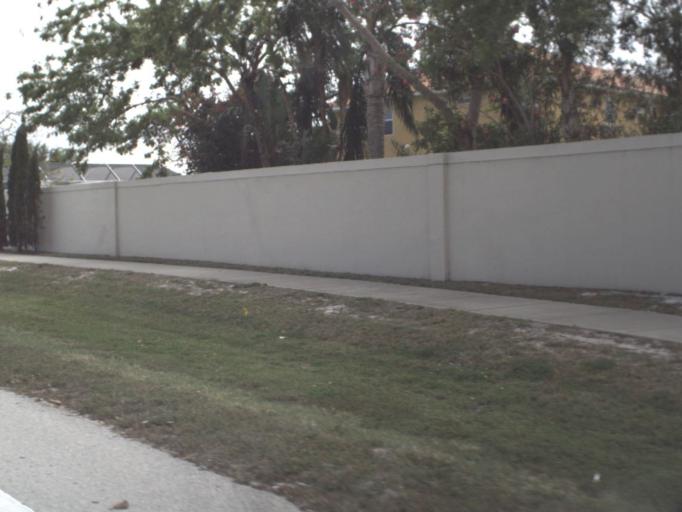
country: US
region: Florida
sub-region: Brevard County
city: Satellite Beach
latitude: 28.1699
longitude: -80.6060
